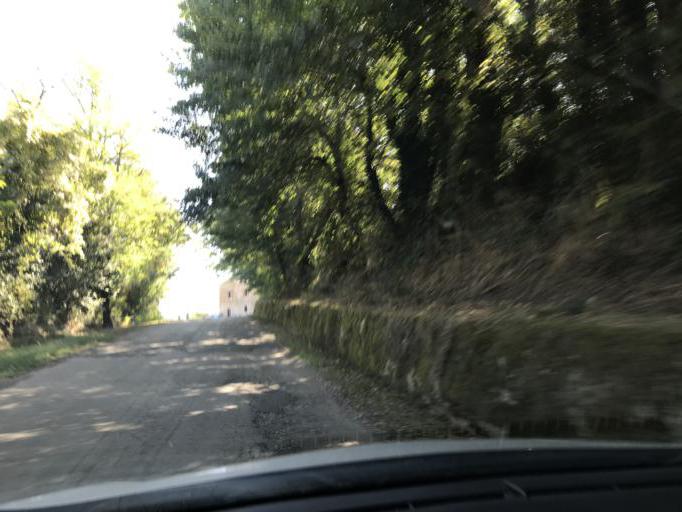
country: IT
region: Umbria
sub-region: Provincia di Terni
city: Avigliano Umbro
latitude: 42.6170
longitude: 12.4118
